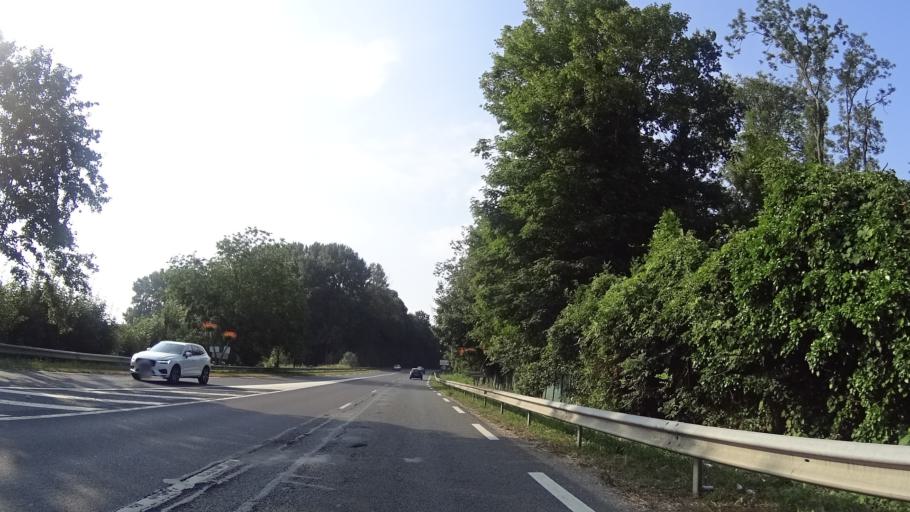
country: FR
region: Ile-de-France
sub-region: Departement du Val-d'Oise
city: Luzarches
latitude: 49.1177
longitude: 2.4282
